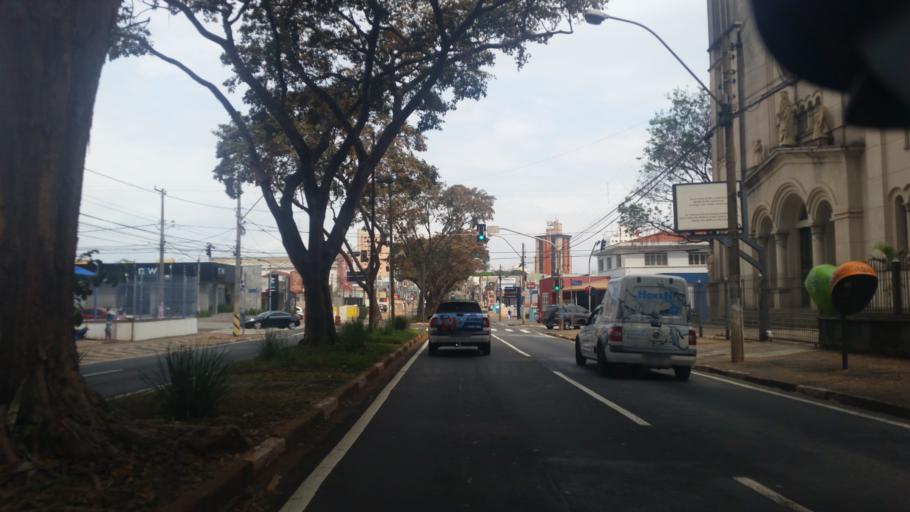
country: BR
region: Sao Paulo
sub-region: Campinas
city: Campinas
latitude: -22.8852
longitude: -47.0747
